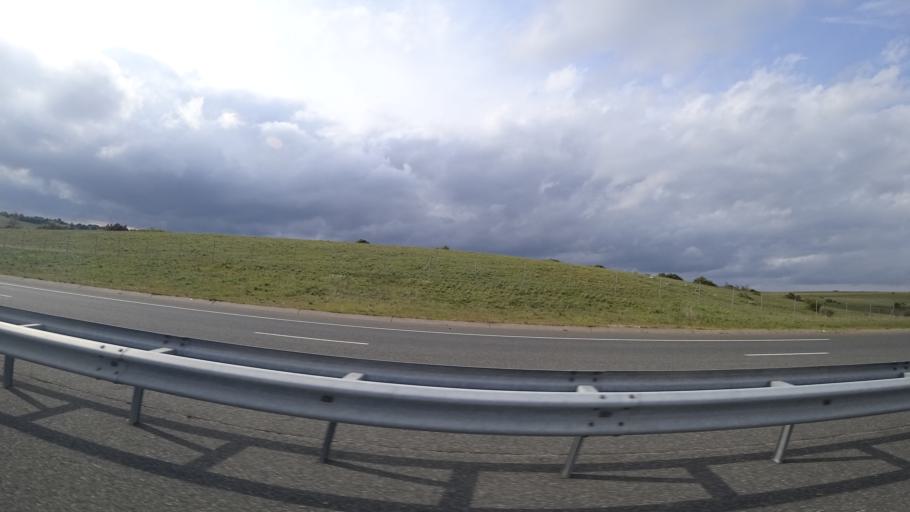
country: FR
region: Midi-Pyrenees
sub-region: Departement de l'Aveyron
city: Creissels
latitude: 44.0279
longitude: 3.0926
